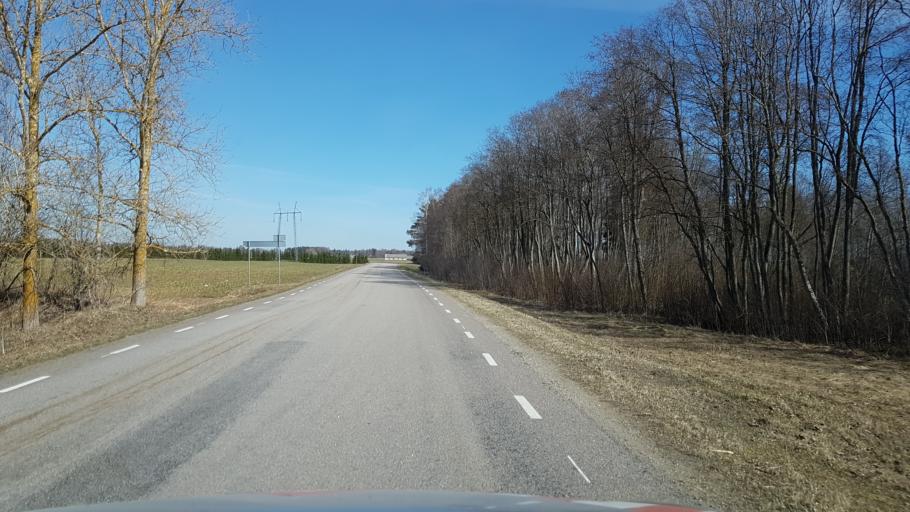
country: EE
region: Laeaene-Virumaa
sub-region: Vinni vald
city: Vinni
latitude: 59.2430
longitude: 26.3519
